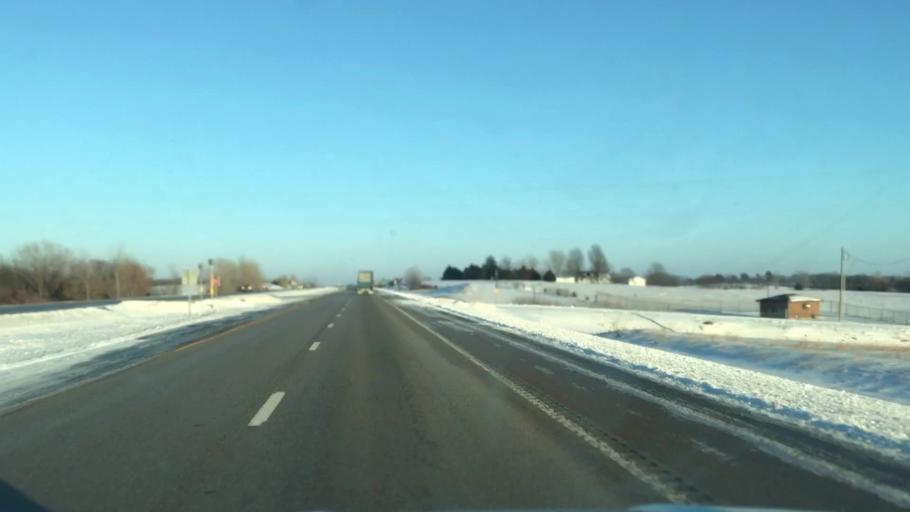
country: US
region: Missouri
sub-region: Clinton County
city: Gower
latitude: 39.7470
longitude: -94.6187
